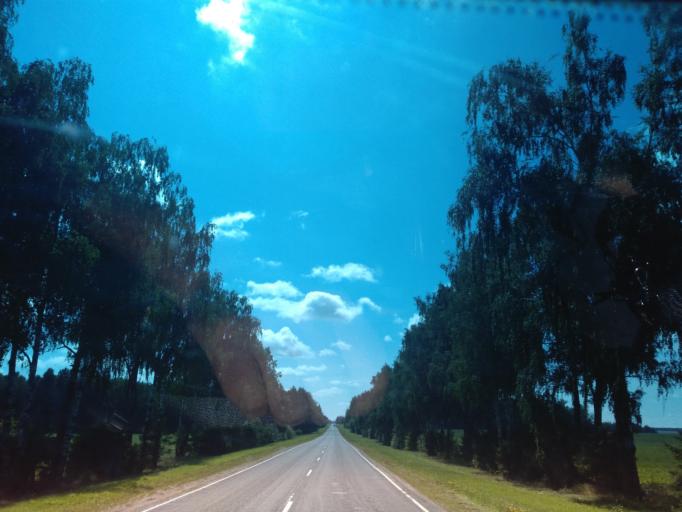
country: BY
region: Minsk
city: Uzda
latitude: 53.3452
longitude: 27.2275
